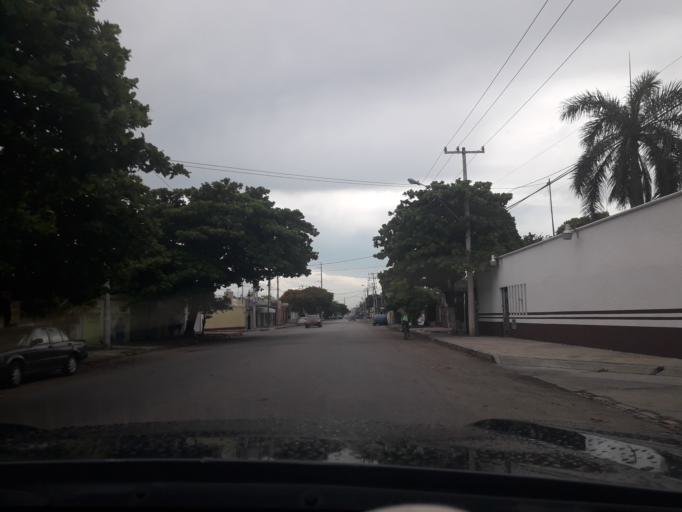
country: MX
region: Yucatan
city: Merida
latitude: 20.9586
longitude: -89.6472
